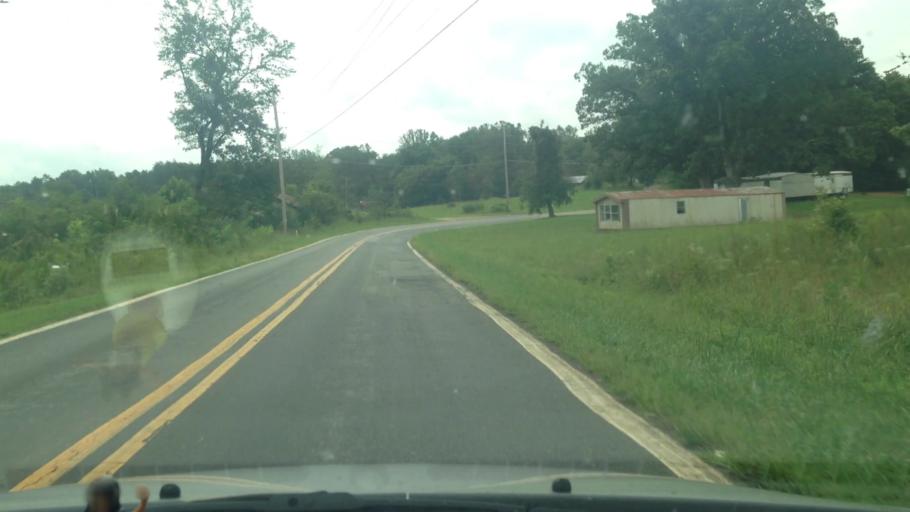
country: US
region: North Carolina
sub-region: Stokes County
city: Danbury
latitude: 36.3858
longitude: -80.1348
